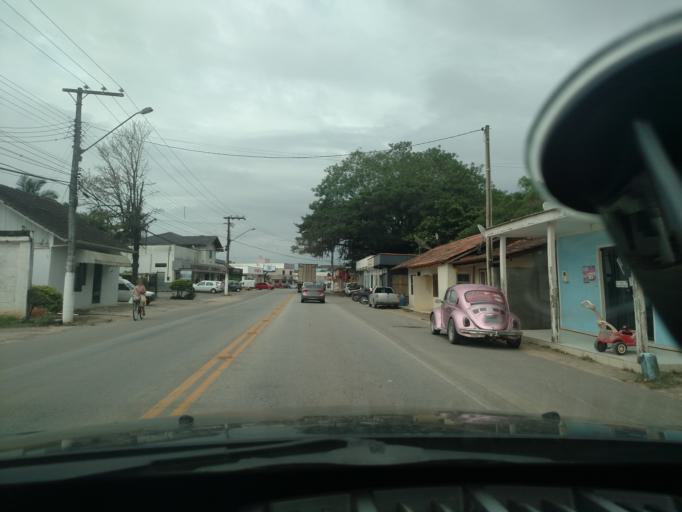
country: BR
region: Santa Catarina
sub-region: Gaspar
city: Gaspar
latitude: -26.8976
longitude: -48.8253
